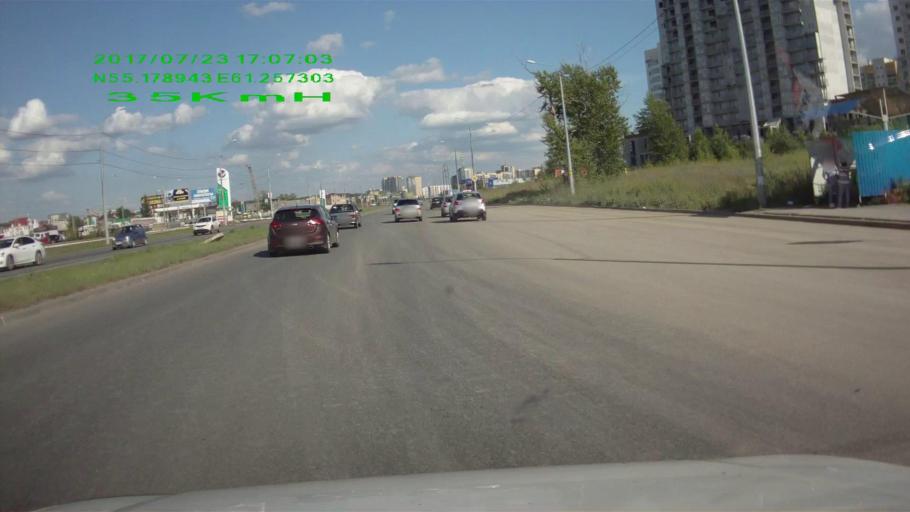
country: RU
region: Chelyabinsk
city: Roshchino
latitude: 55.1787
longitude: 61.2583
